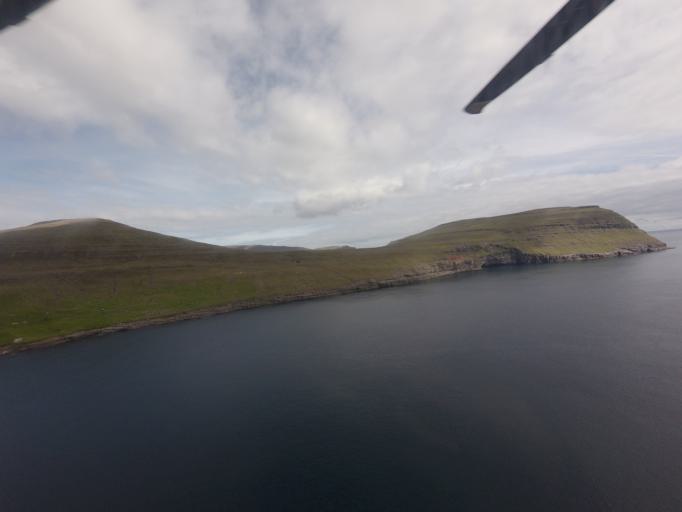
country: FO
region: Nordoyar
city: Klaksvik
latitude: 62.2742
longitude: -6.3293
